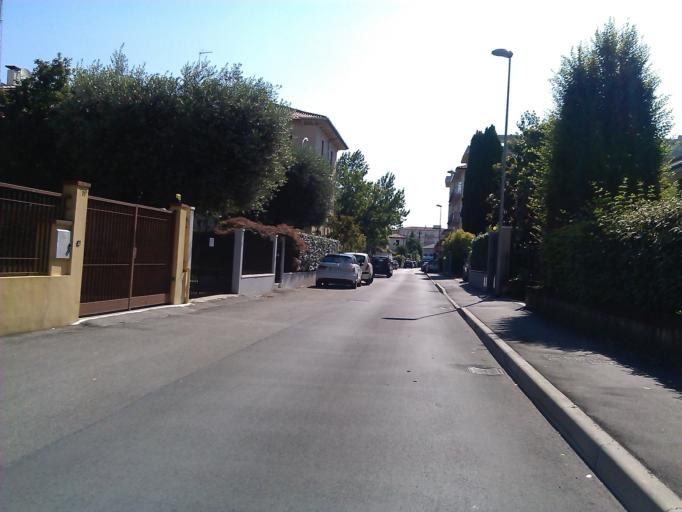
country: IT
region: Veneto
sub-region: Provincia di Vicenza
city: San Zeno-San Giuseppe
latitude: 45.7704
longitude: 11.7503
